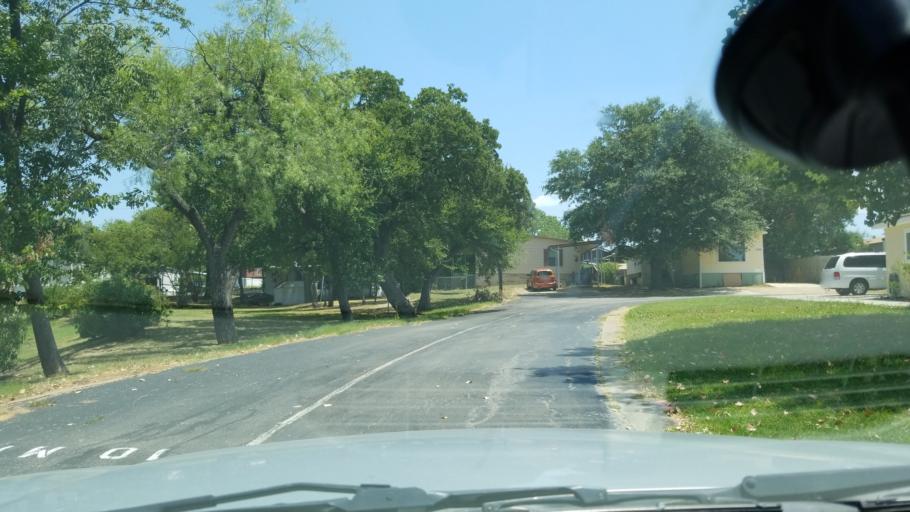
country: US
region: Texas
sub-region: Dallas County
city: Irving
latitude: 32.8253
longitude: -96.9961
